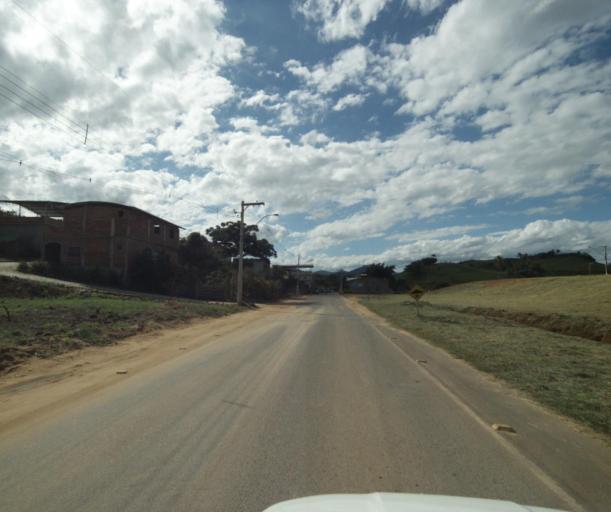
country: BR
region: Espirito Santo
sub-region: Sao Jose Do Calcado
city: Sao Jose do Calcado
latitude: -21.0414
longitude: -41.6522
